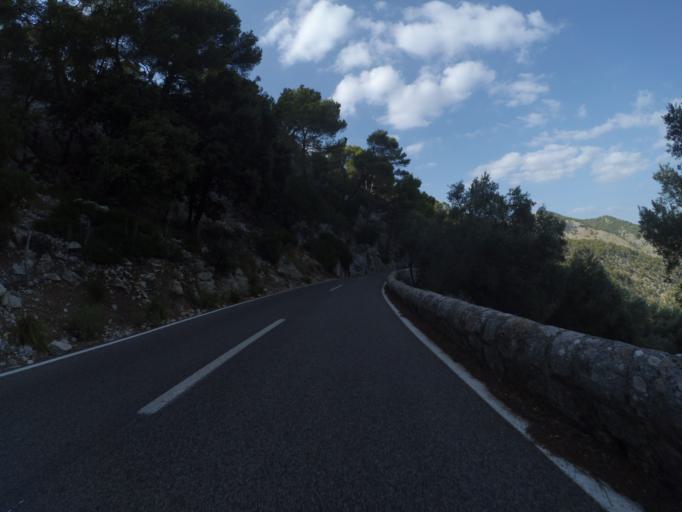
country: ES
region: Balearic Islands
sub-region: Illes Balears
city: Selva
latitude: 39.7917
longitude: 2.8944
